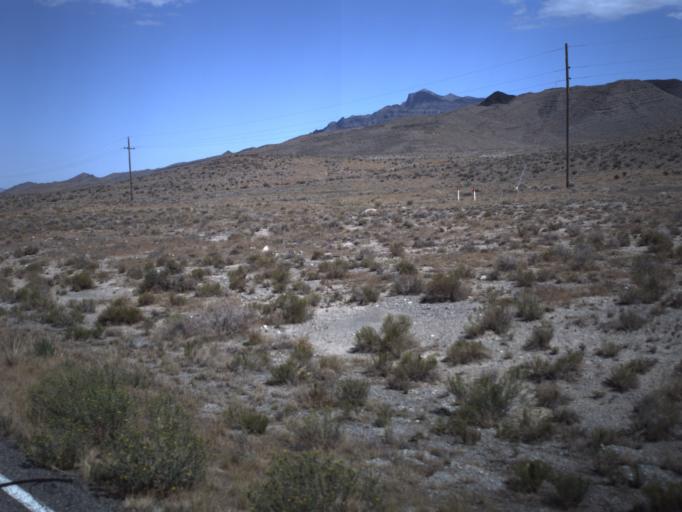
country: US
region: Utah
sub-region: Beaver County
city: Milford
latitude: 39.0237
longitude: -113.3689
